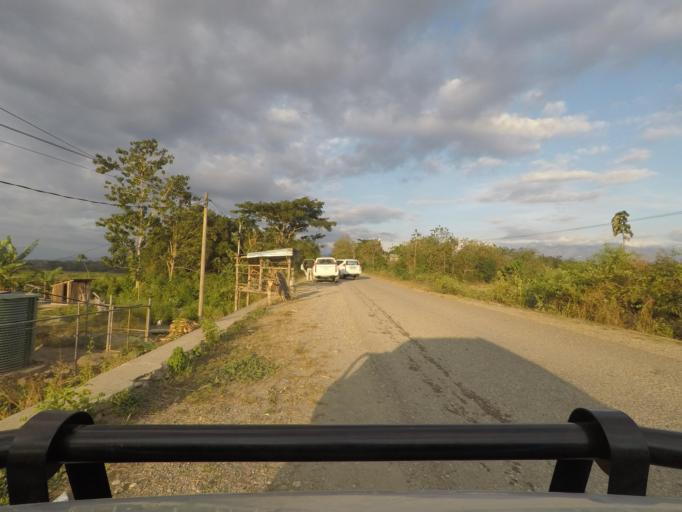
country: TL
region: Bobonaro
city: Maliana
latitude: -8.9614
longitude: 125.1147
